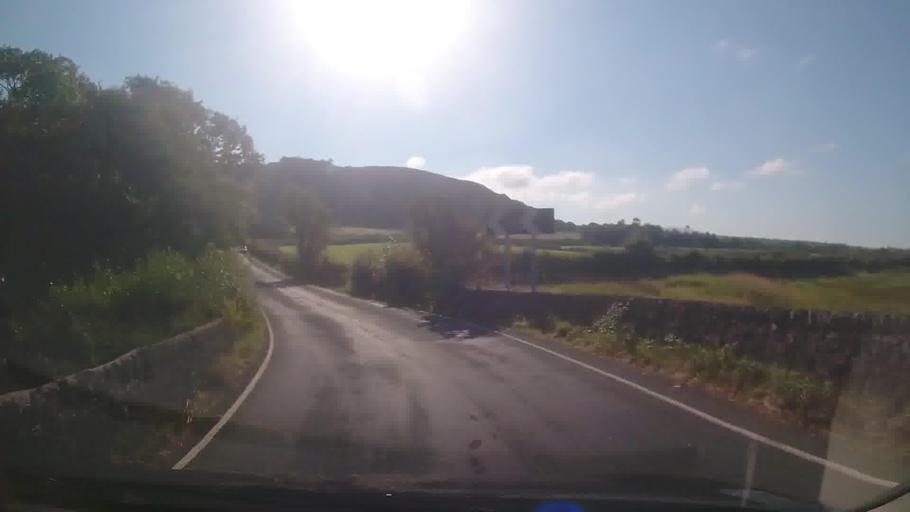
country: GB
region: England
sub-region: Cumbria
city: Seascale
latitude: 54.3556
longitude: -3.3671
